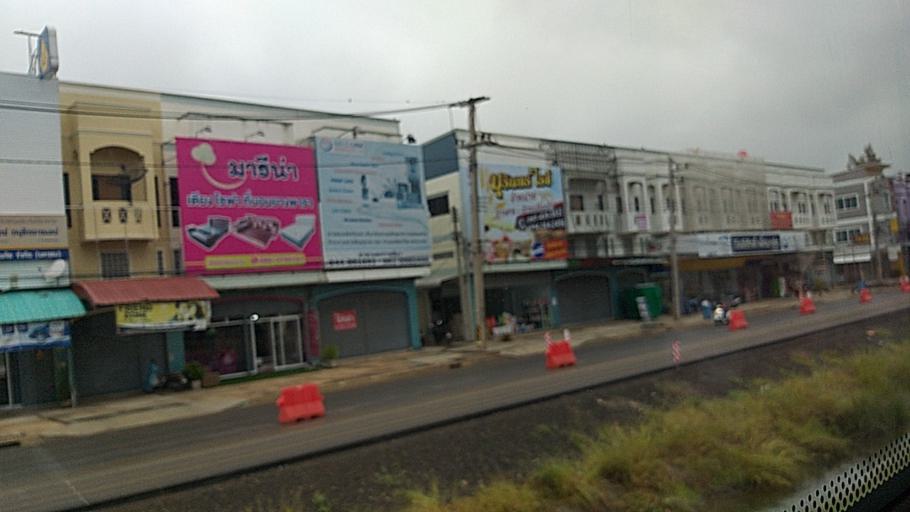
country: TH
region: Nakhon Ratchasima
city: Nakhon Ratchasima
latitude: 14.9951
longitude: 102.0781
